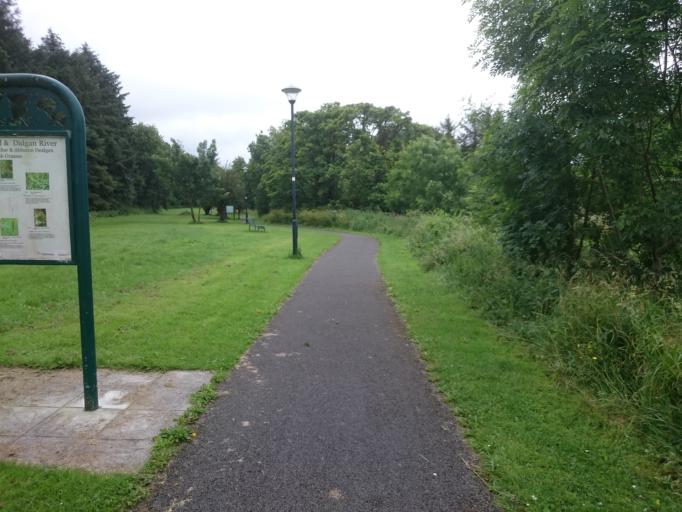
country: IE
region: Connaught
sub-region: Maigh Eo
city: Ballyhaunis
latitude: 53.7645
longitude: -8.7628
